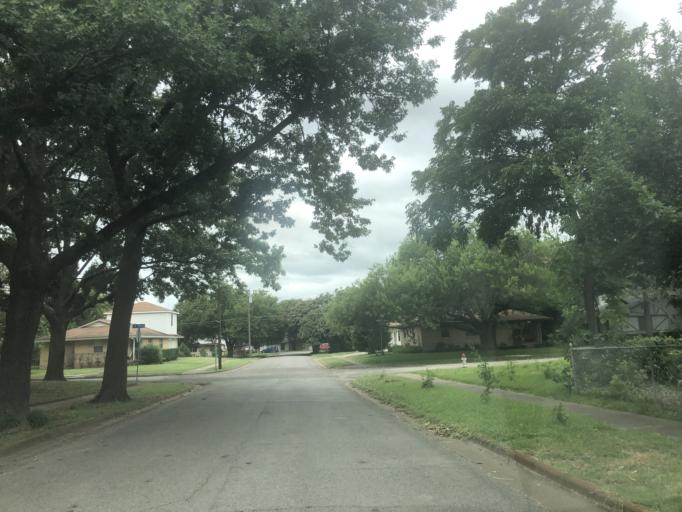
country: US
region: Texas
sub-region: Dallas County
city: Duncanville
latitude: 32.6545
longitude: -96.9151
